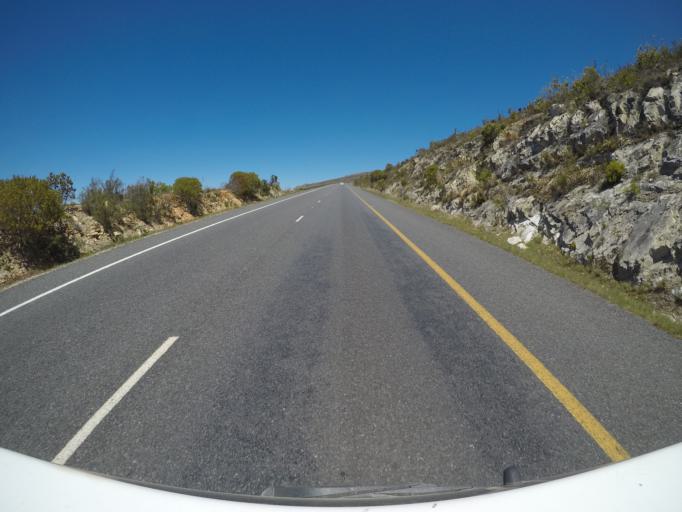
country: ZA
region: Western Cape
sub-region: Overberg District Municipality
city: Grabouw
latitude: -34.2199
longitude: 19.1847
